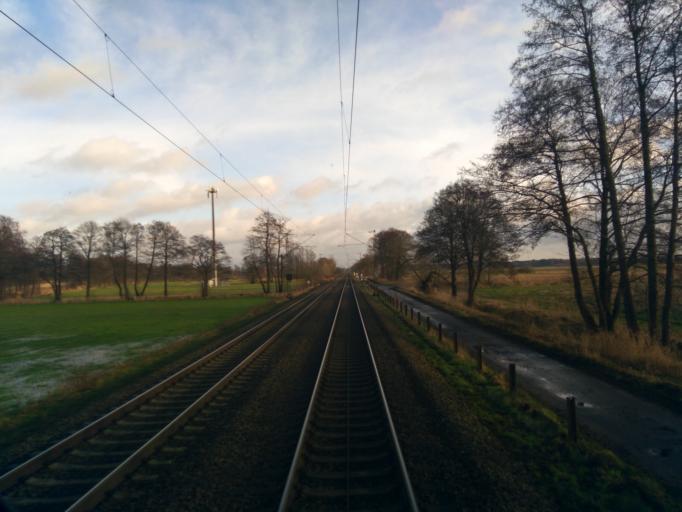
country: DE
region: Lower Saxony
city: Hassendorf
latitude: 53.1017
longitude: 9.2706
